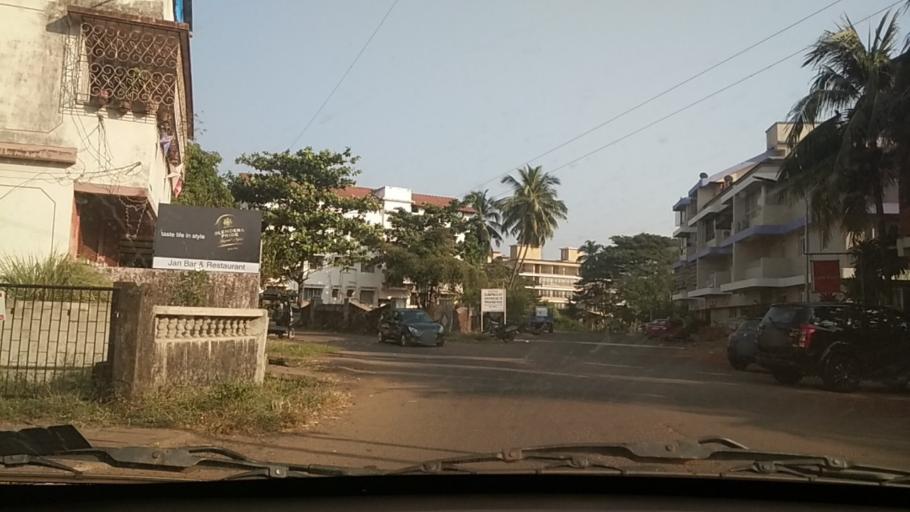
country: IN
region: Goa
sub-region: North Goa
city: Panaji
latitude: 15.4803
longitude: 73.8138
